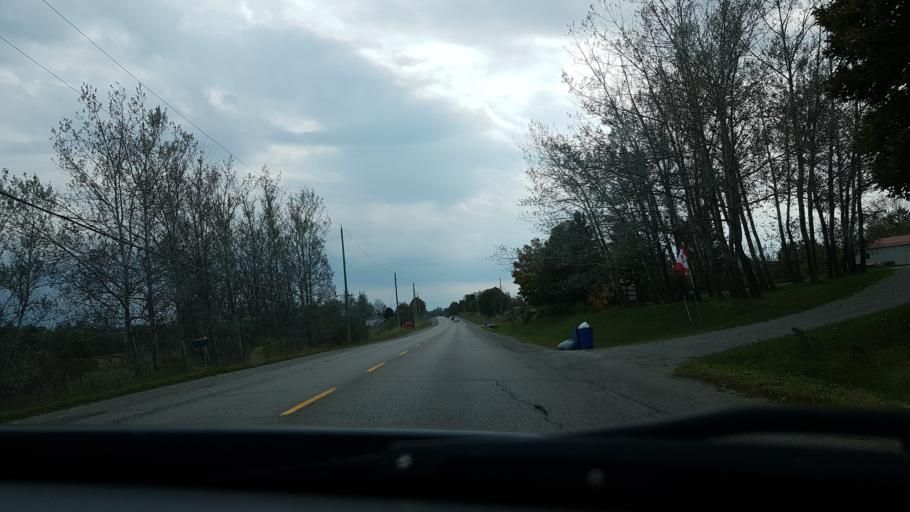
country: CA
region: Ontario
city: Omemee
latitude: 44.4997
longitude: -78.7429
